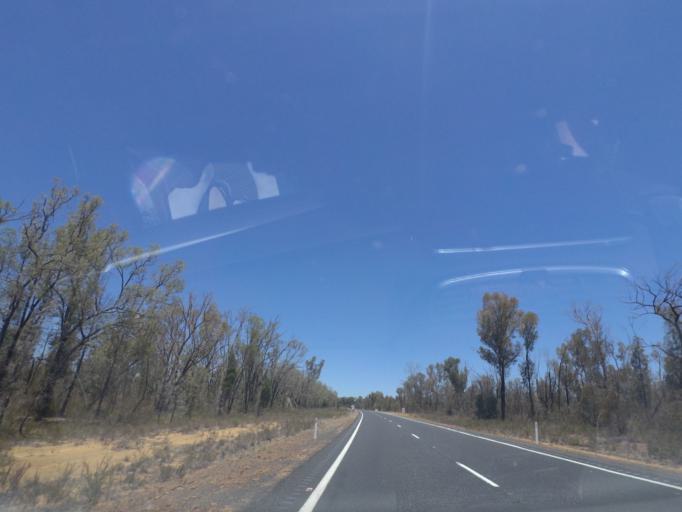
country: AU
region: New South Wales
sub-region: Warrumbungle Shire
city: Coonabarabran
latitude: -30.9410
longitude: 149.4239
